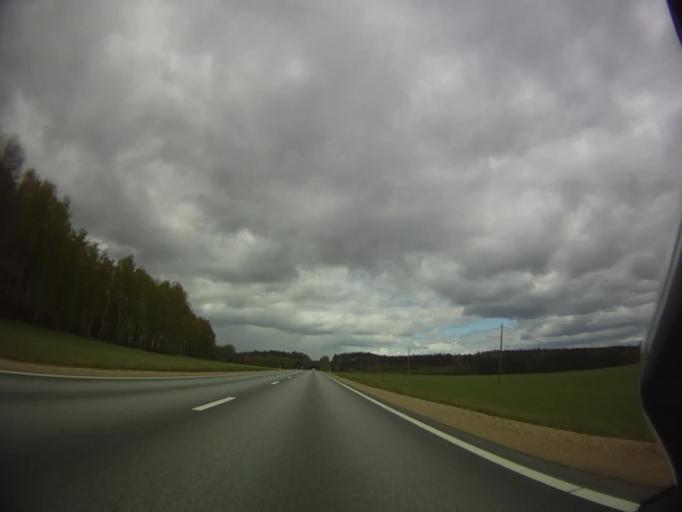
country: LV
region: Sigulda
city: Sigulda
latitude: 57.2709
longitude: 24.8898
